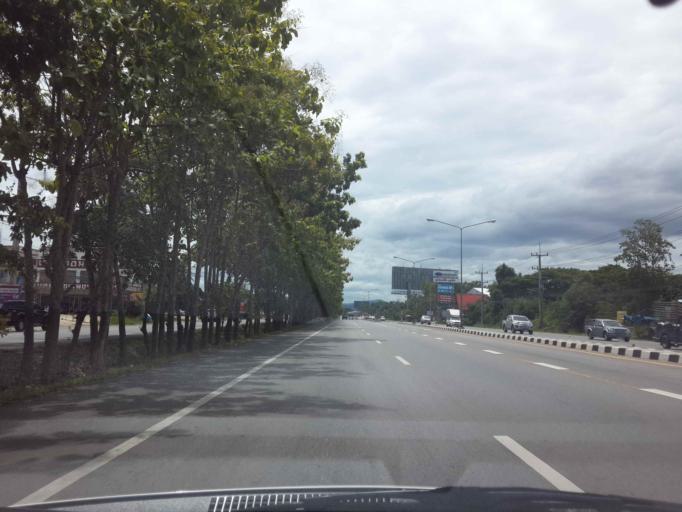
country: TH
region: Phetchaburi
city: Phetchaburi
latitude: 13.1233
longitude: 99.8864
